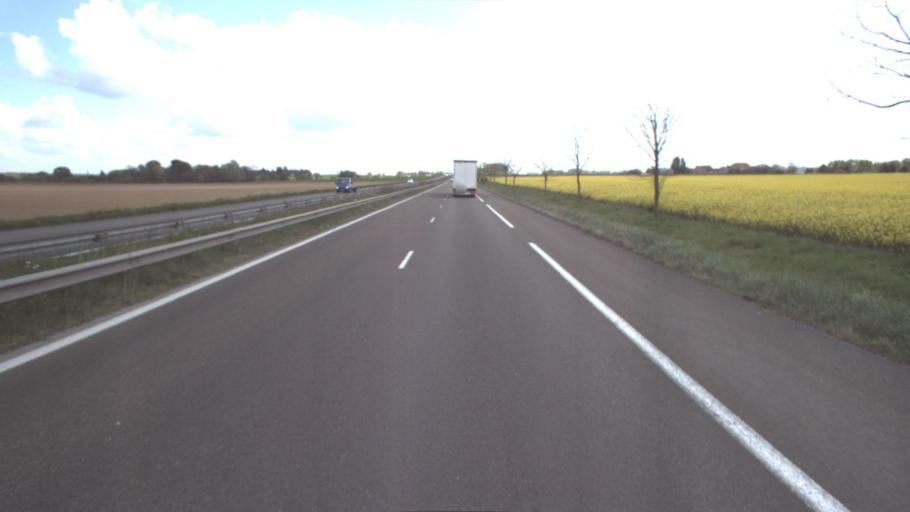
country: FR
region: Ile-de-France
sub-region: Departement de Seine-et-Marne
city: Rozay-en-Brie
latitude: 48.6863
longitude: 2.9866
